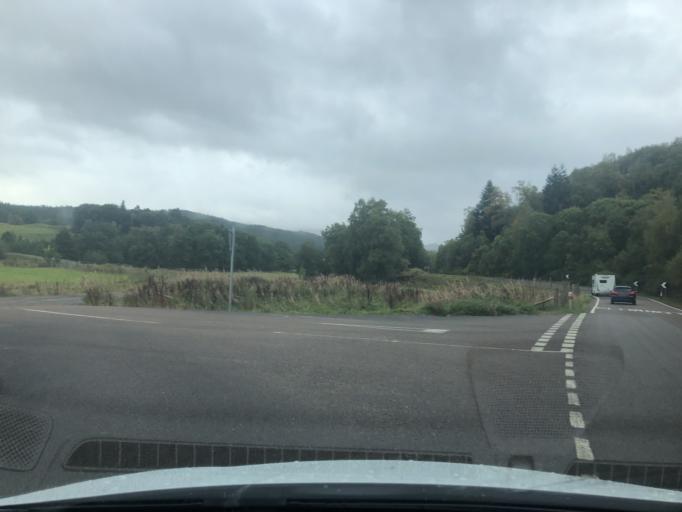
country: GB
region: Scotland
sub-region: Highland
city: Kingussie
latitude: 56.9771
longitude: -4.3794
